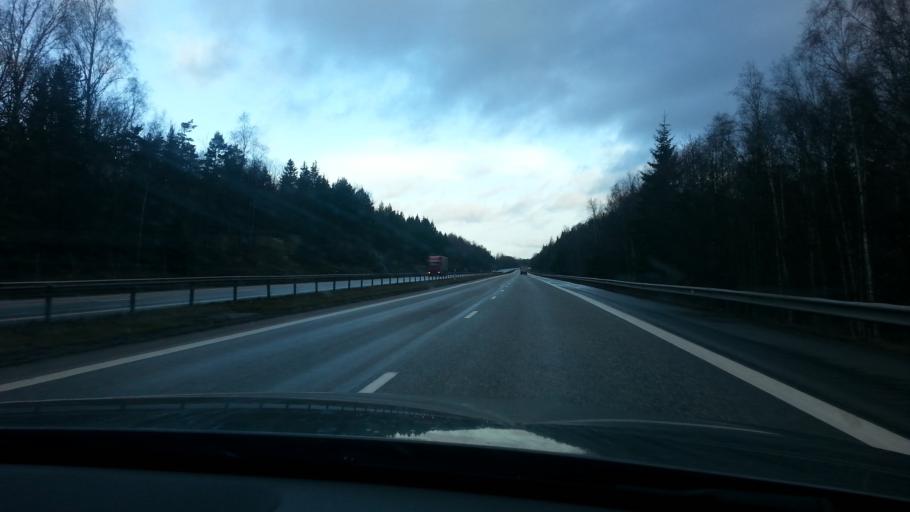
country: SE
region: OEstergoetland
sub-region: Odeshogs Kommun
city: OEdeshoeg
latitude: 58.1590
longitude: 14.5814
